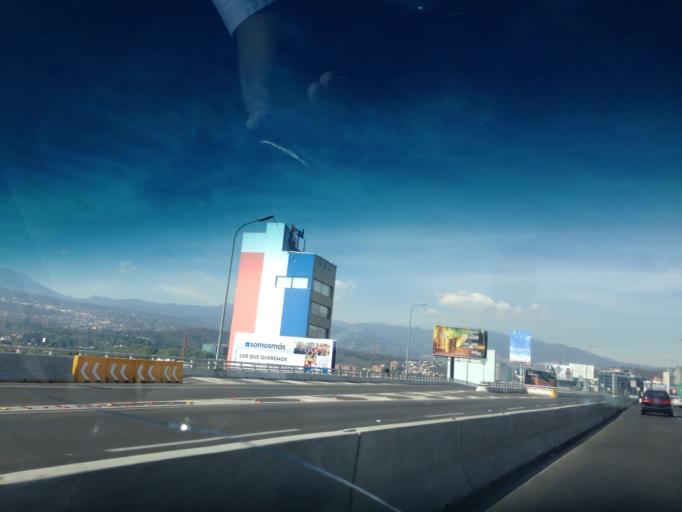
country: MX
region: Mexico City
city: Tlalpan
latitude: 19.3028
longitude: -99.1728
